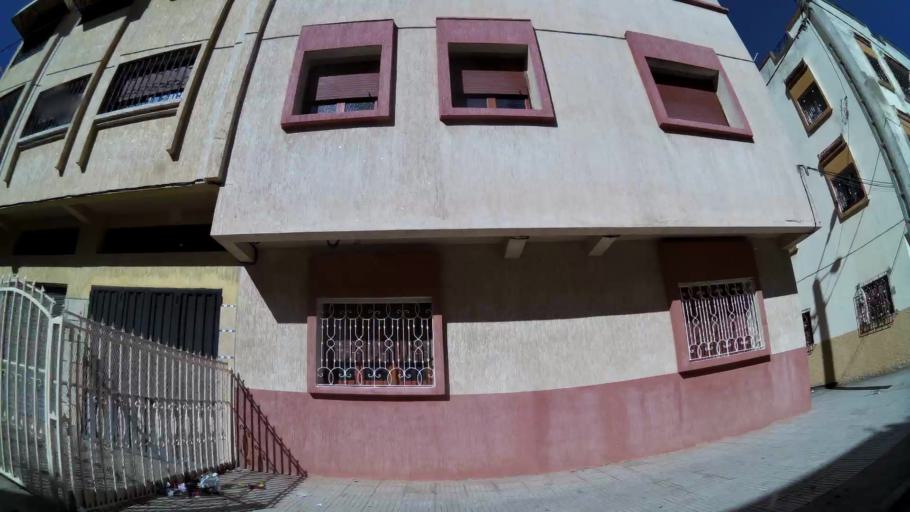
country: MA
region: Meknes-Tafilalet
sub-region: Meknes
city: Meknes
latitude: 33.8965
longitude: -5.5002
